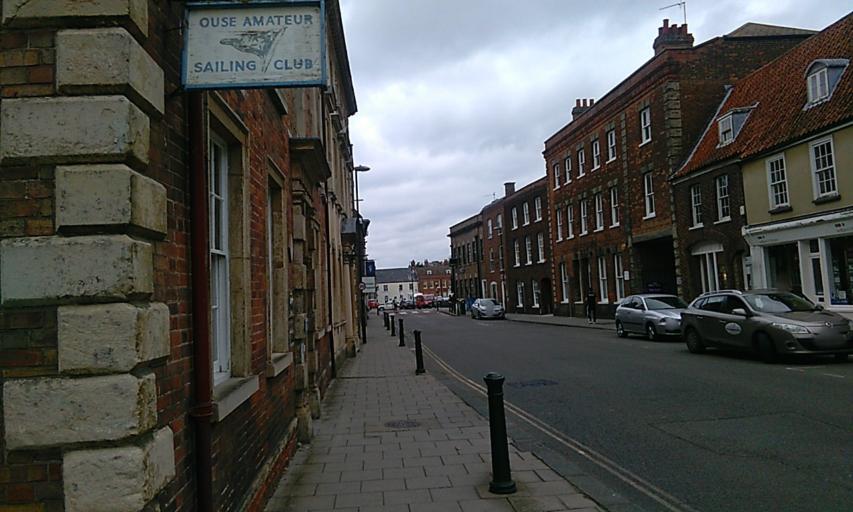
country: GB
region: England
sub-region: Norfolk
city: King's Lynn
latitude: 52.7551
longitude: 0.3936
